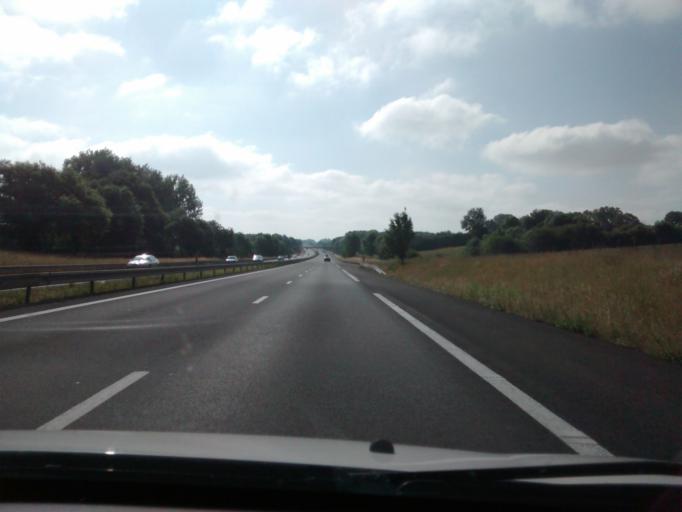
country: FR
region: Pays de la Loire
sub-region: Departement de la Mayenne
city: Soulge-sur-Ouette
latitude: 48.0649
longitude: -0.5367
